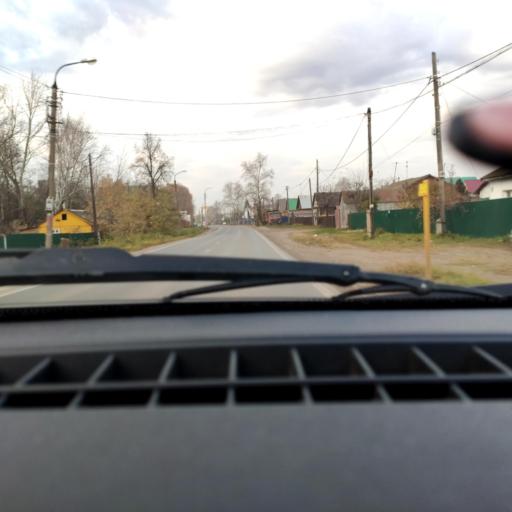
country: RU
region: Bashkortostan
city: Ufa
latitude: 54.8177
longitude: 56.1686
